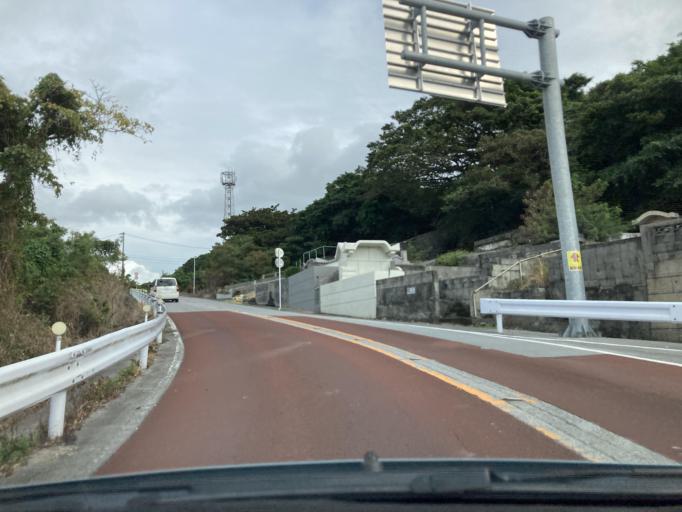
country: JP
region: Okinawa
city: Itoman
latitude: 26.1229
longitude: 127.6773
